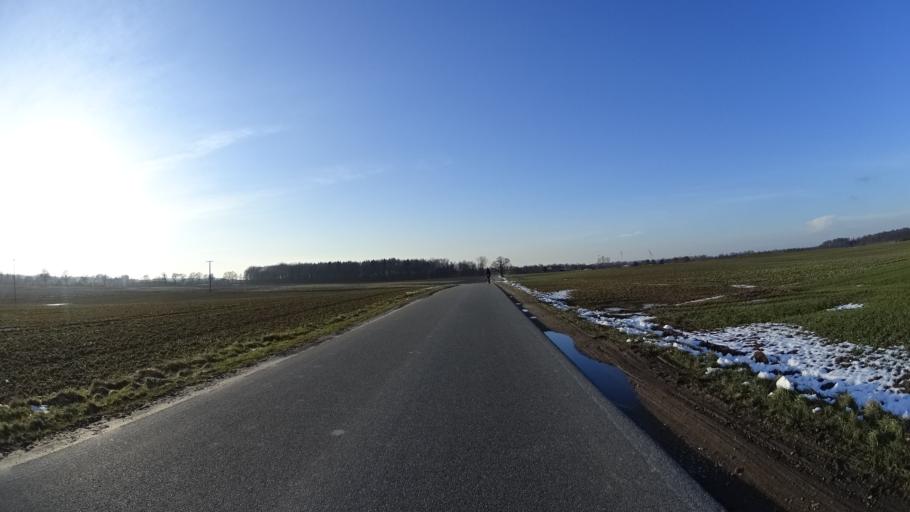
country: DE
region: Schleswig-Holstein
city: Fargau-Pratjau
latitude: 54.3342
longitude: 10.4138
